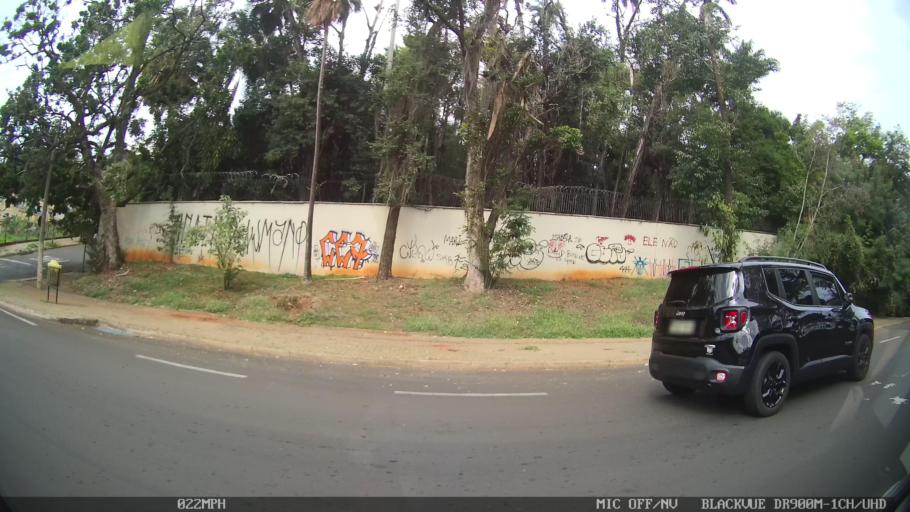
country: BR
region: Sao Paulo
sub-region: Piracicaba
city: Piracicaba
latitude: -22.7194
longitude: -47.6546
